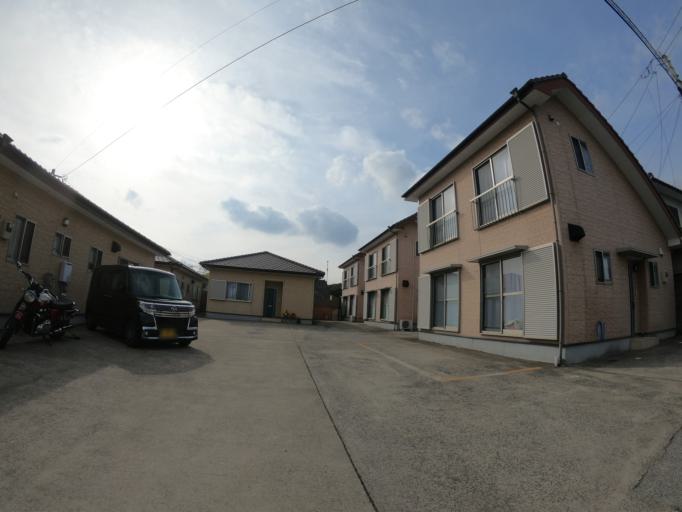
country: JP
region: Nagasaki
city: Shimabara
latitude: 32.6682
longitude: 130.3016
